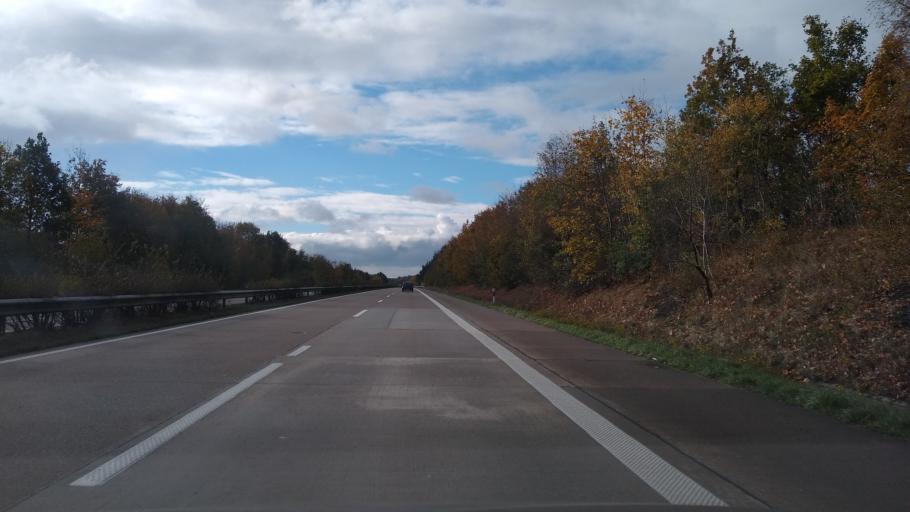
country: DE
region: Lower Saxony
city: Wardenburg
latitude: 53.0736
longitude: 8.2450
